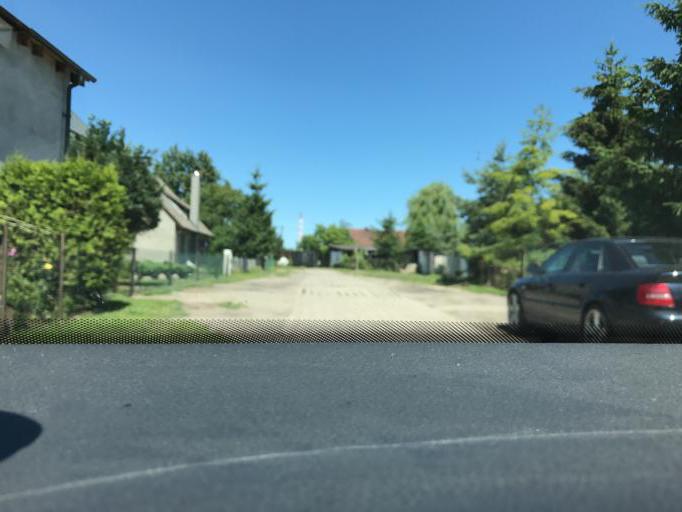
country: PL
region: Pomeranian Voivodeship
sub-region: Gdansk
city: Gdansk
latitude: 54.3309
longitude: 18.7453
